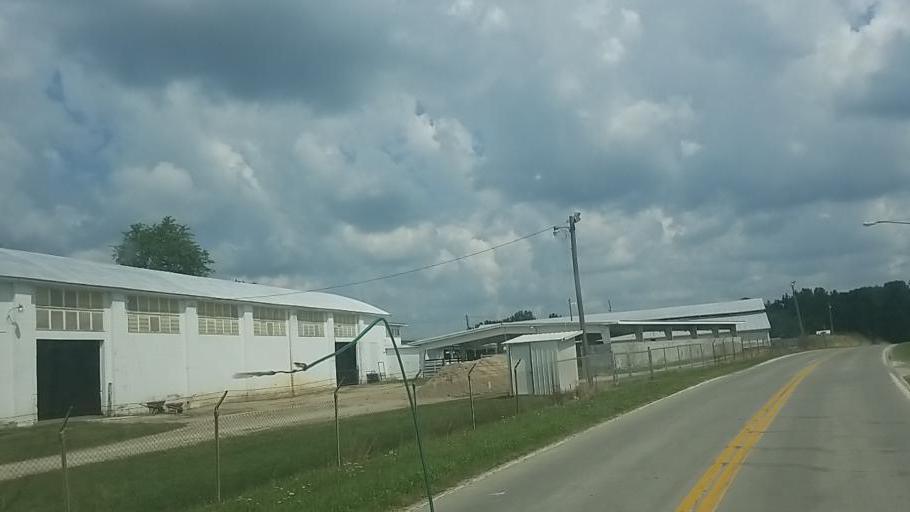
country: US
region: Ohio
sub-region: Wyandot County
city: Upper Sandusky
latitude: 40.8442
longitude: -83.2776
